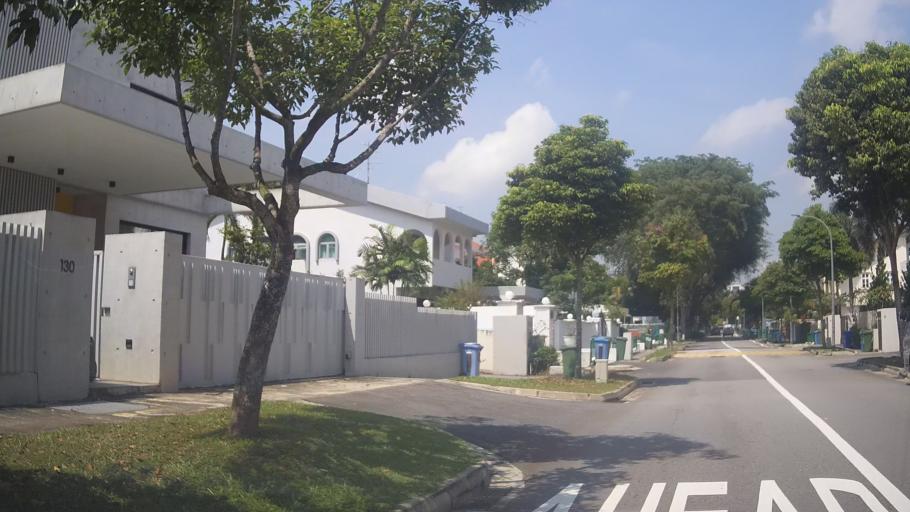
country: SG
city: Singapore
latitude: 1.3226
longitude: 103.7990
